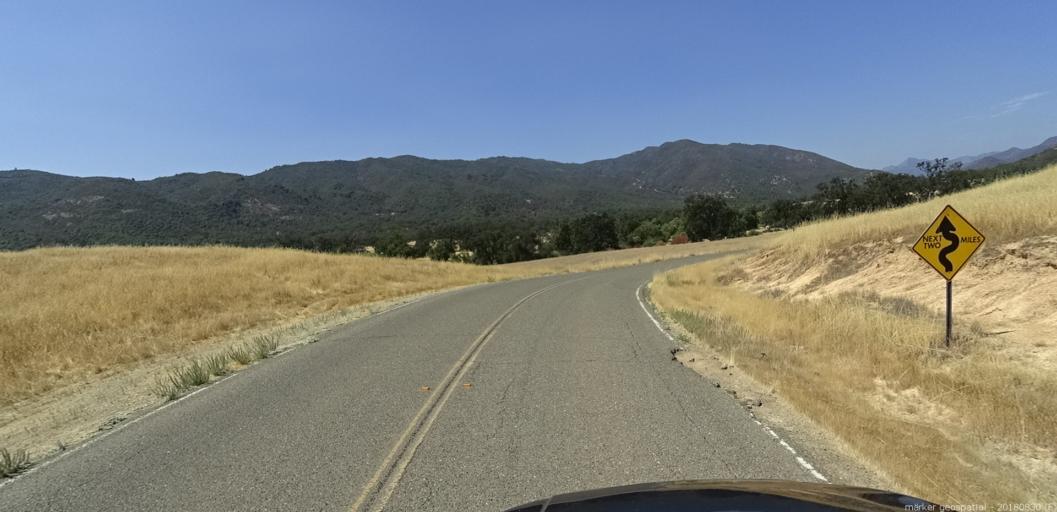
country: US
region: California
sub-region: Monterey County
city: King City
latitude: 35.9738
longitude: -121.3324
